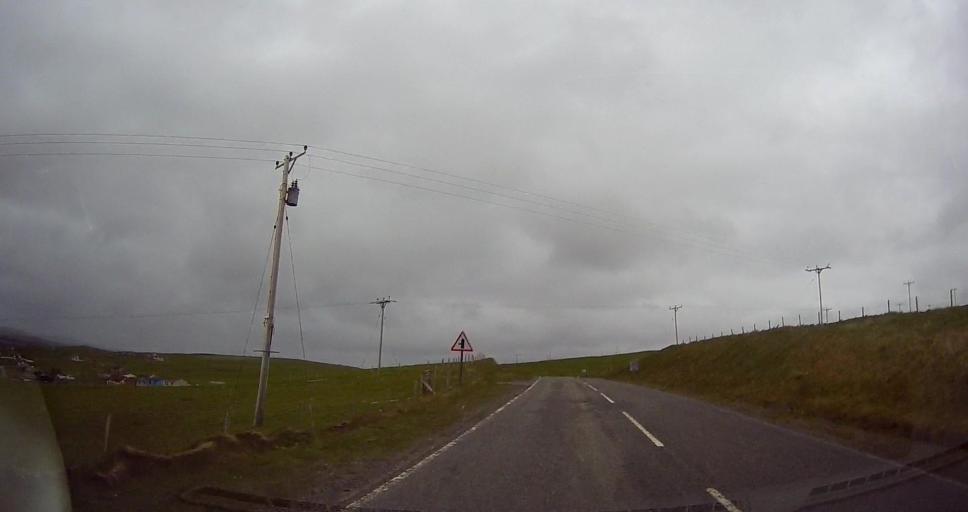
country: GB
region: Scotland
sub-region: Shetland Islands
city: Lerwick
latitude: 60.2588
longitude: -1.4078
